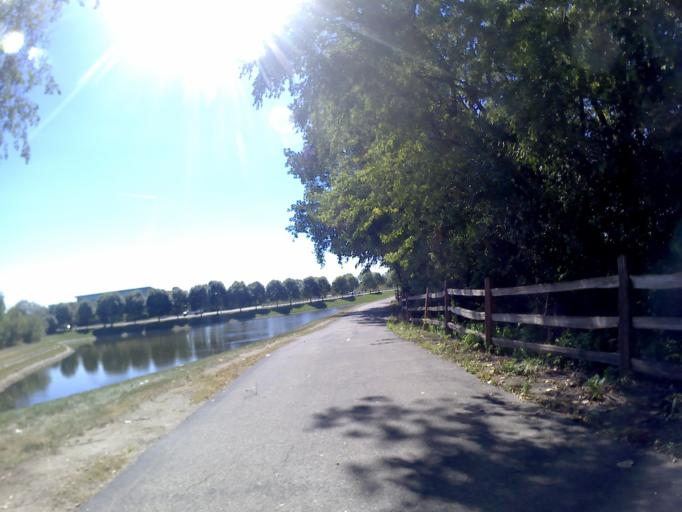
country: US
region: Illinois
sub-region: DuPage County
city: Warrenville
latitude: 41.8095
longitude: -88.1745
